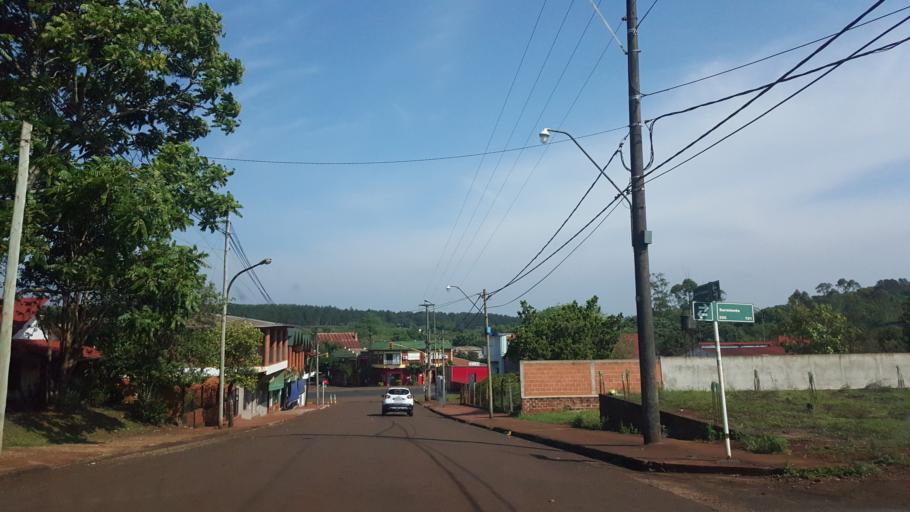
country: AR
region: Misiones
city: Capiovi
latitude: -26.9260
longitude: -55.0591
